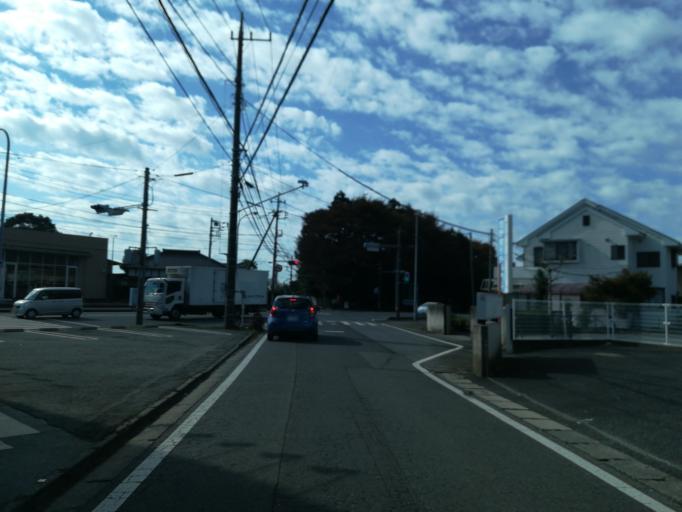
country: JP
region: Ibaraki
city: Naka
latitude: 36.0719
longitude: 140.0917
